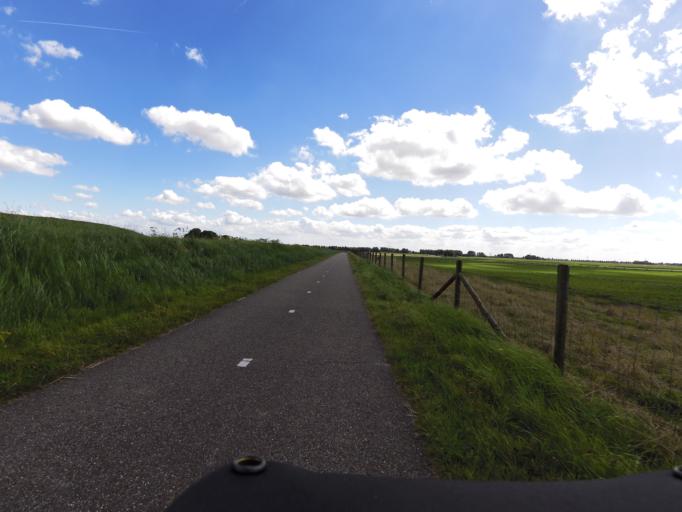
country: NL
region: South Holland
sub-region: Gemeente Oud-Beijerland
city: Oud-Beijerland
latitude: 51.8367
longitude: 4.3788
